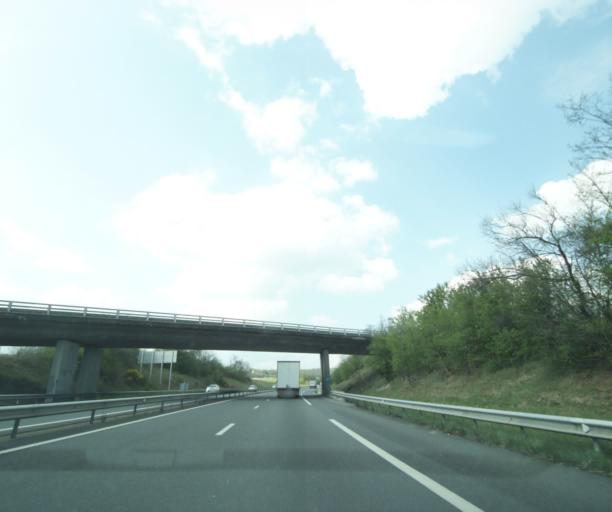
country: FR
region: Auvergne
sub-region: Departement du Puy-de-Dome
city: Saint-Bonnet-pres-Riom
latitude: 45.9534
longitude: 3.1073
